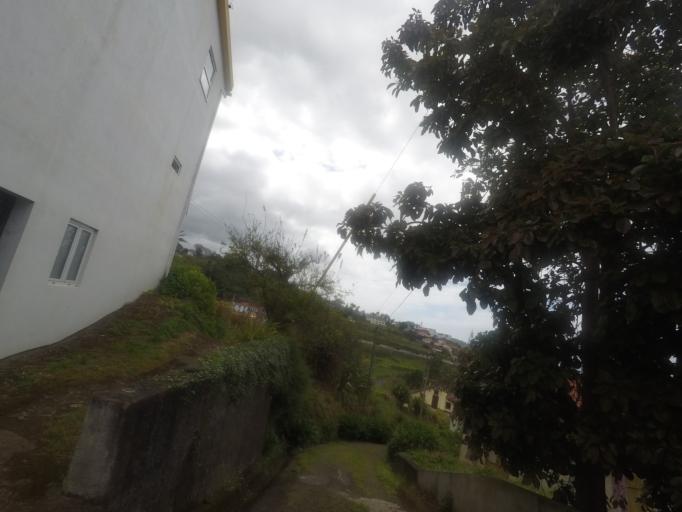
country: PT
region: Madeira
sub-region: Santana
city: Santana
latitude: 32.8077
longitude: -16.8819
